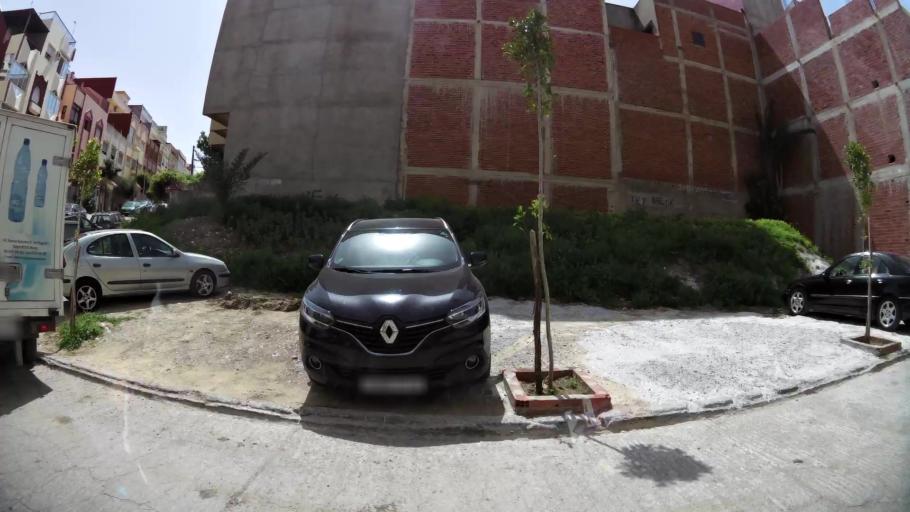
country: MA
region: Tanger-Tetouan
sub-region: Tanger-Assilah
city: Tangier
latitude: 35.7600
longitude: -5.8333
